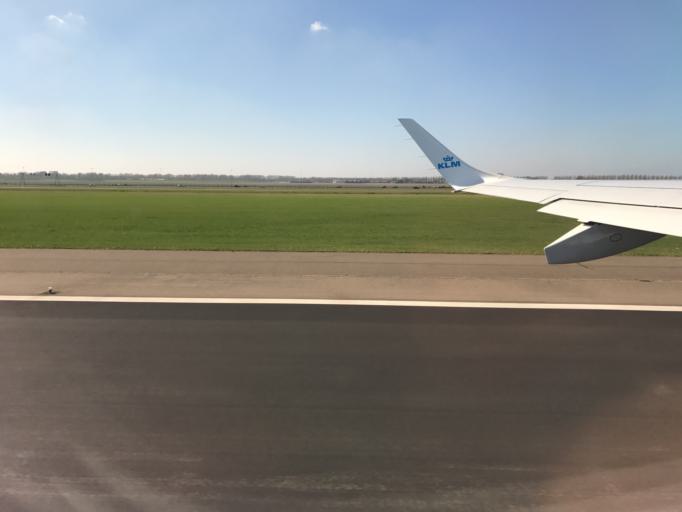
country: NL
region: North Holland
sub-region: Gemeente Haarlemmermeer
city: Hoofddorp
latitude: 52.3148
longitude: 4.7384
